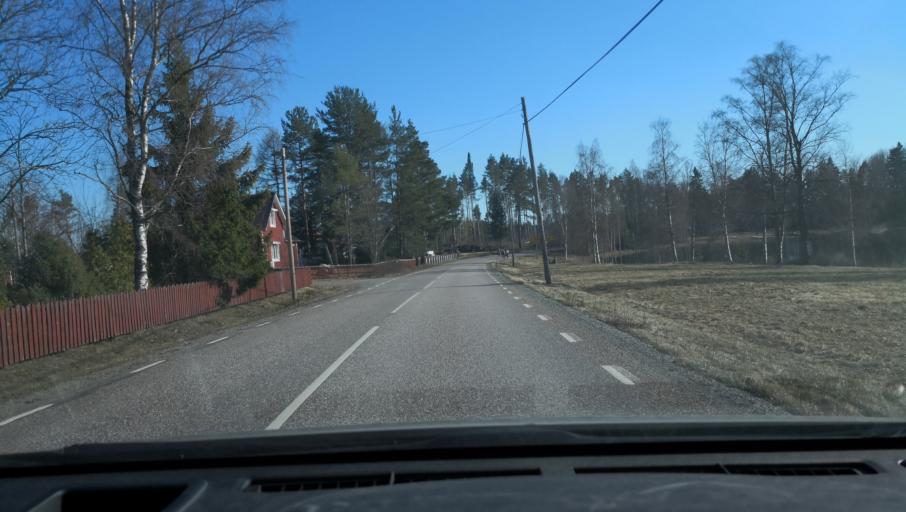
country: SE
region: Dalarna
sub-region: Avesta Kommun
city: Avesta
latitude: 60.0004
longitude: 16.3471
